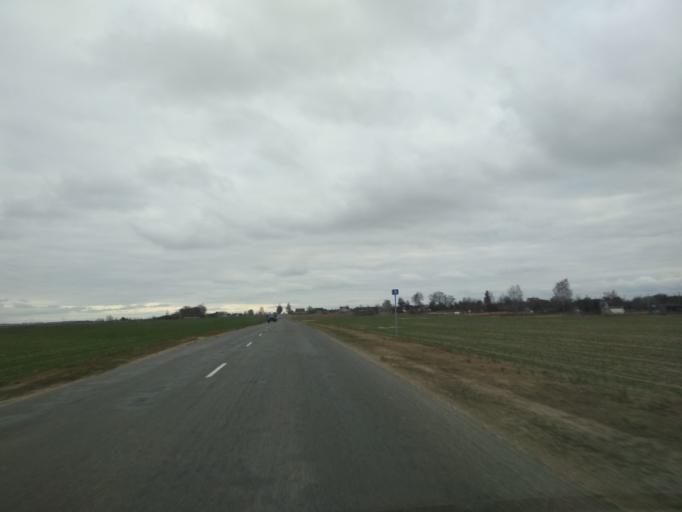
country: BY
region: Minsk
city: Svislach
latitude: 53.5700
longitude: 27.9944
